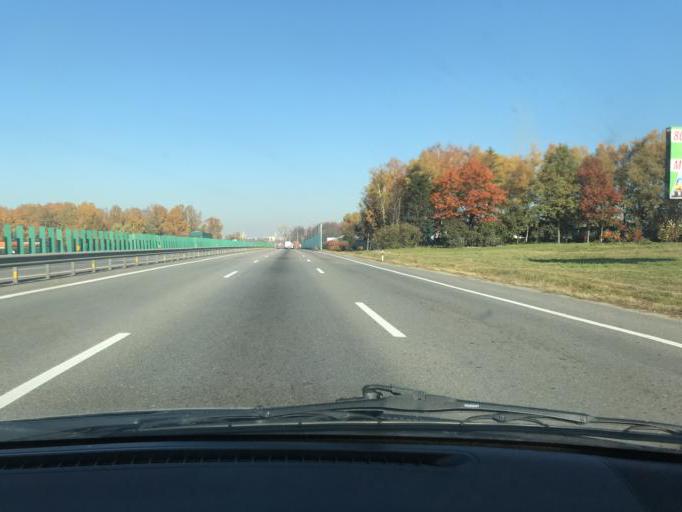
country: BY
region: Minsk
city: Syenitsa
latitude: 53.8211
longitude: 27.5320
